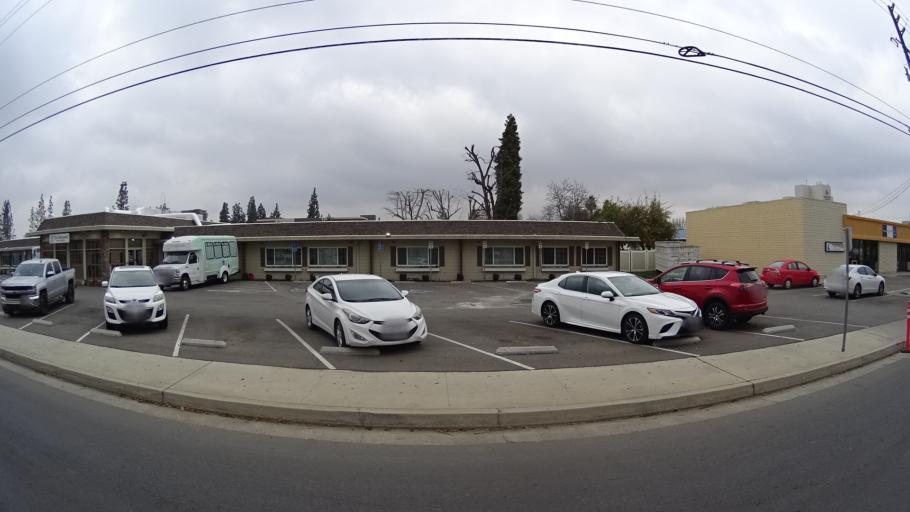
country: US
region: California
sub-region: Kern County
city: Bakersfield
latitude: 35.3907
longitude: -119.0096
